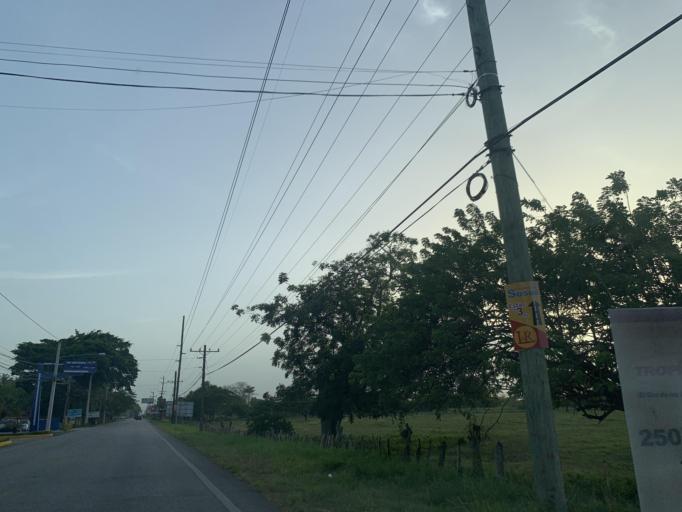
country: DO
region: Puerto Plata
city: Cabarete
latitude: 19.7746
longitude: -70.4926
